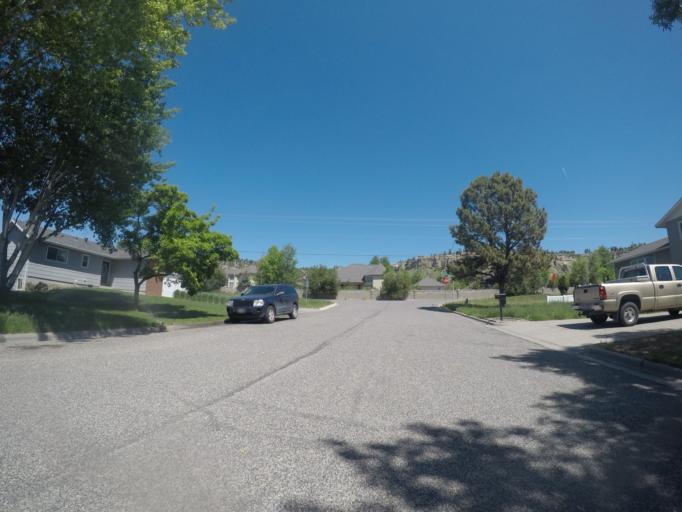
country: US
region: Montana
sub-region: Yellowstone County
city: Billings
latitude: 45.7982
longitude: -108.6055
